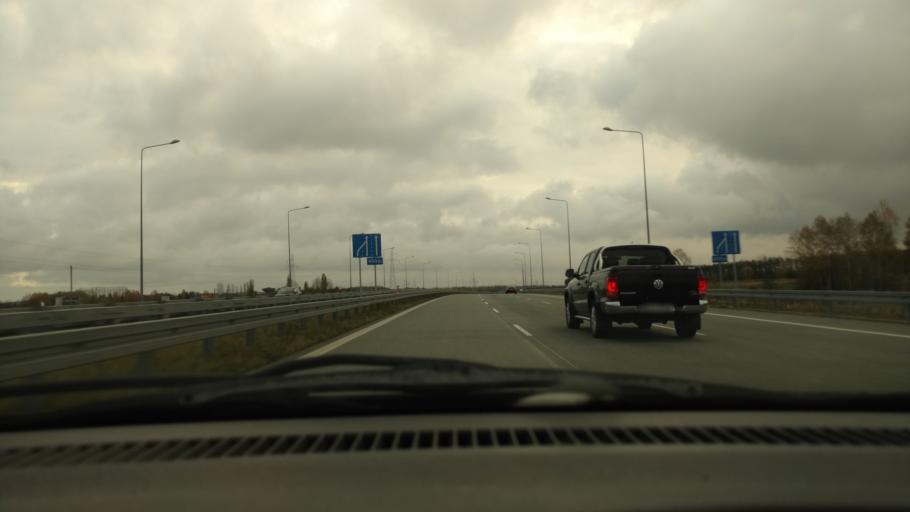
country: PL
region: Lodz Voivodeship
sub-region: Powiat lodzki wschodni
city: Tuszyn
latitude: 51.6437
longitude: 19.5248
